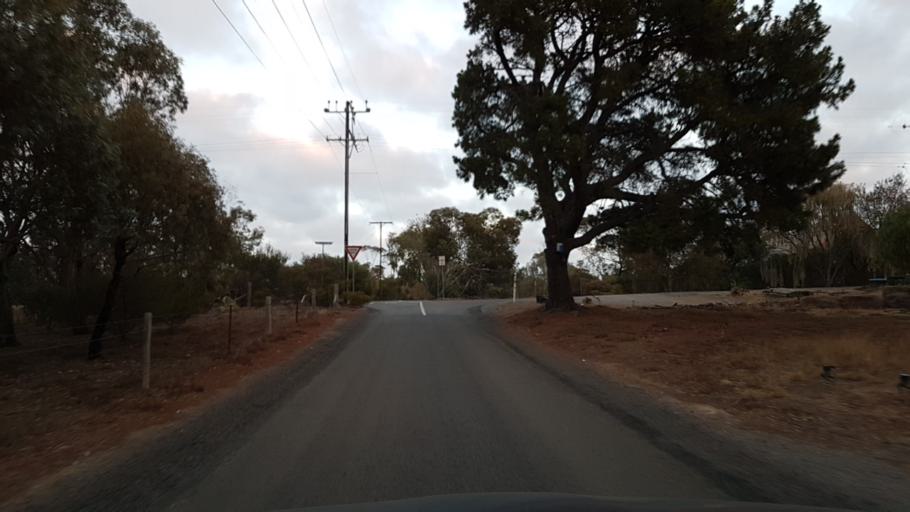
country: AU
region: South Australia
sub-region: Mount Barker
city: Callington
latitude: -35.0688
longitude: 139.0116
